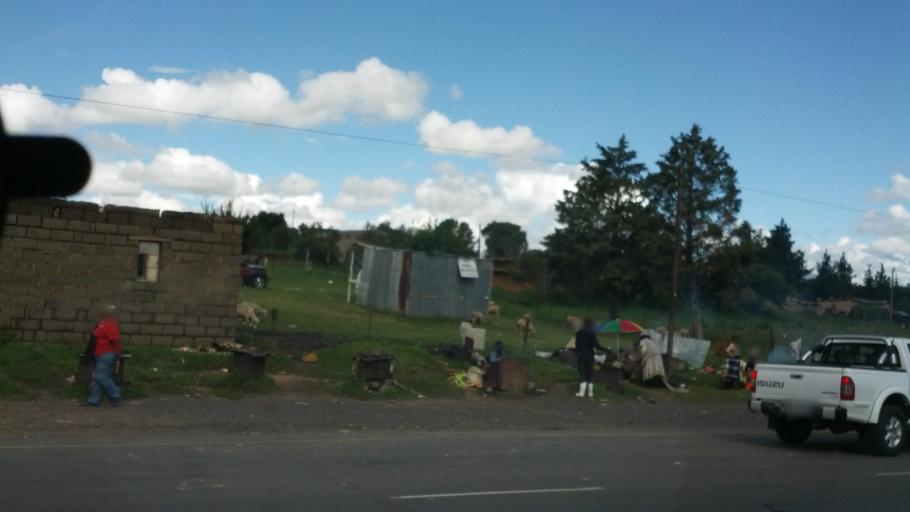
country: LS
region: Maseru
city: Maseru
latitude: -29.4893
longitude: 27.5272
